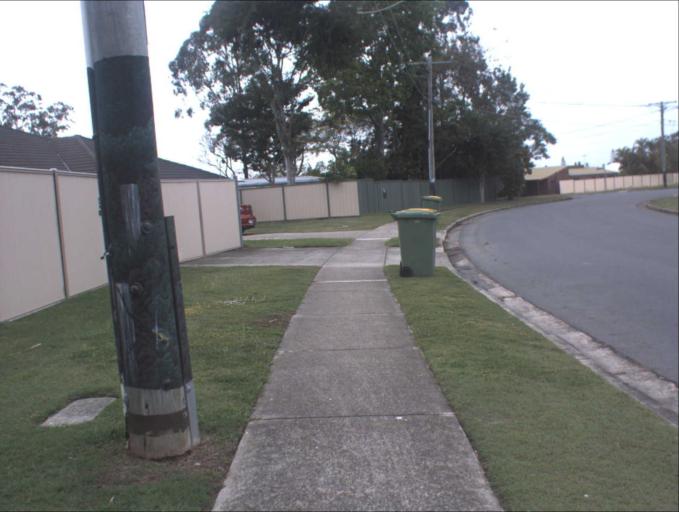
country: AU
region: Queensland
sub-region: Logan
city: Park Ridge South
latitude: -27.6861
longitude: 153.0193
